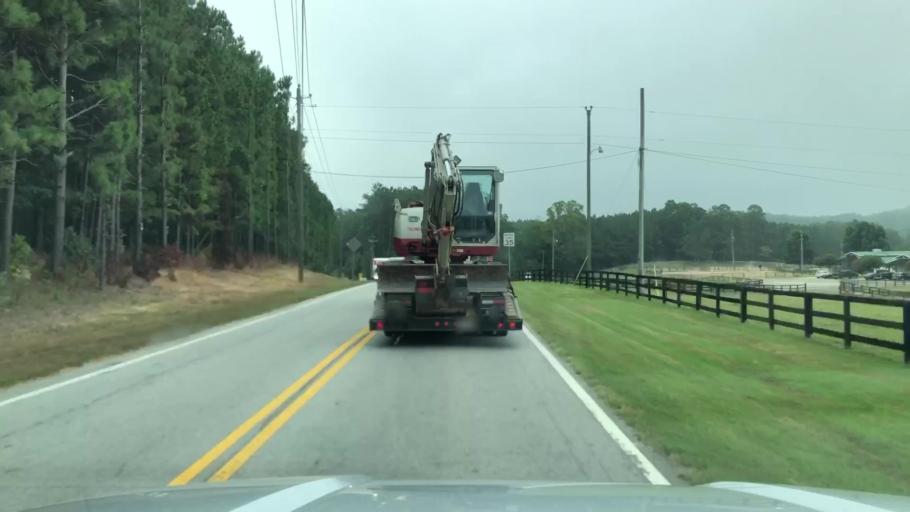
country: US
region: Georgia
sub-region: Bartow County
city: Emerson
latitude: 34.0560
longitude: -84.7999
